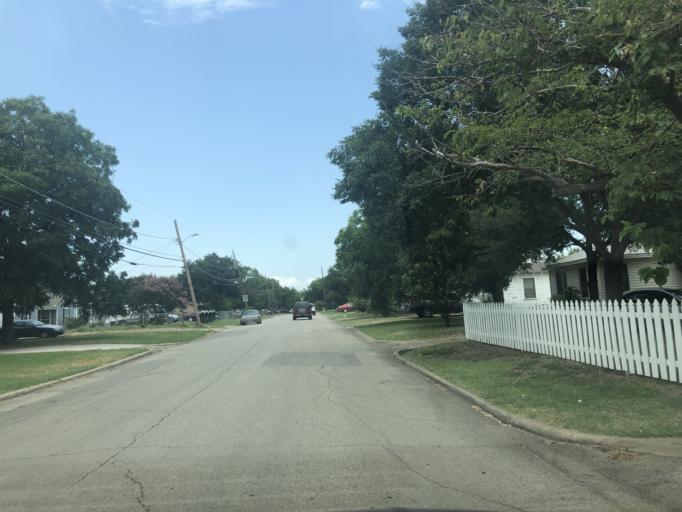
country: US
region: Texas
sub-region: Dallas County
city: Grand Prairie
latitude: 32.7375
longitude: -97.0038
